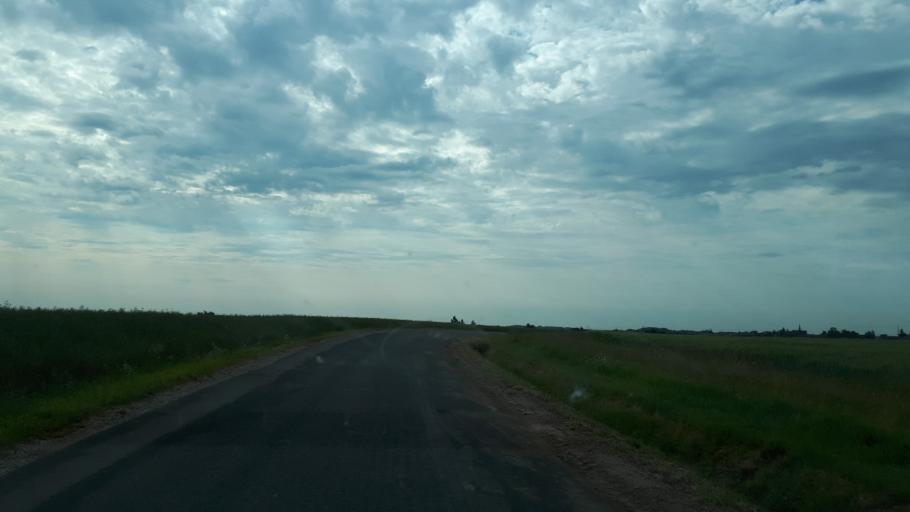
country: FR
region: Centre
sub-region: Departement du Loir-et-Cher
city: Saint-Amand-Longpre
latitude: 47.7328
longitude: 1.0017
